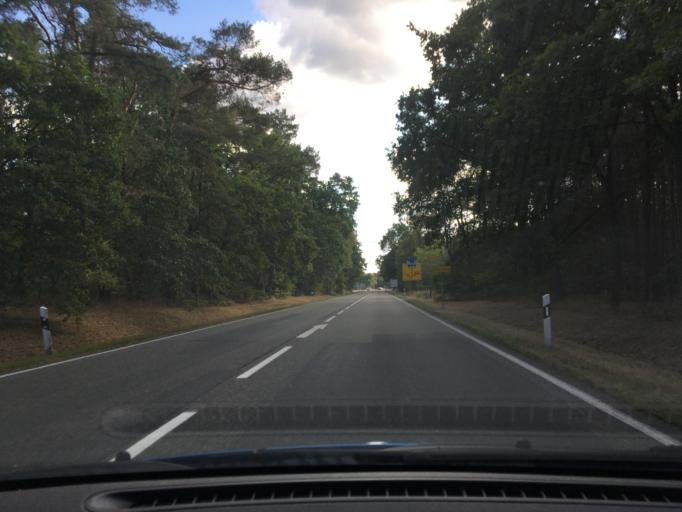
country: DE
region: Mecklenburg-Vorpommern
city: Gross Laasch
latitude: 53.3567
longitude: 11.5420
